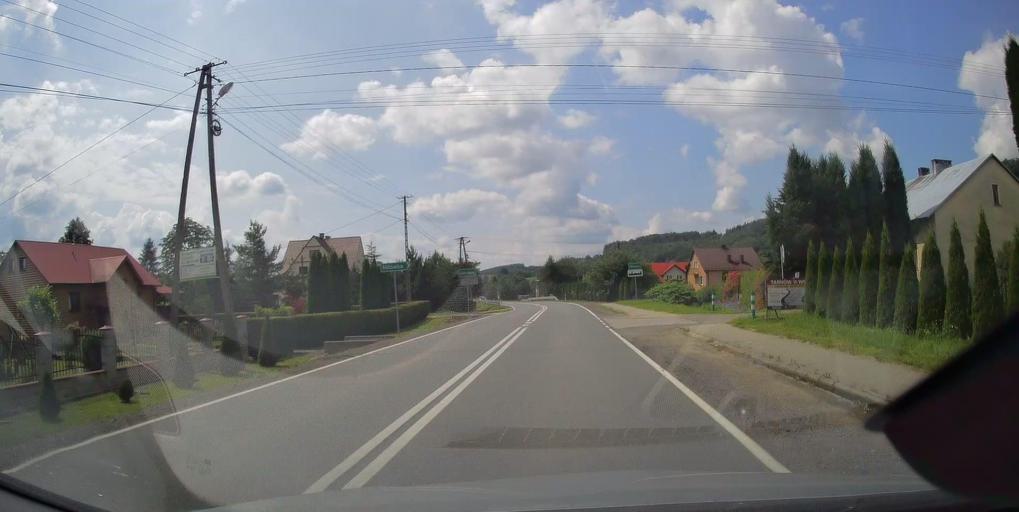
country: PL
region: Lesser Poland Voivodeship
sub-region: Powiat tarnowski
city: Wielka Wies
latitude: 49.9019
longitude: 20.8155
